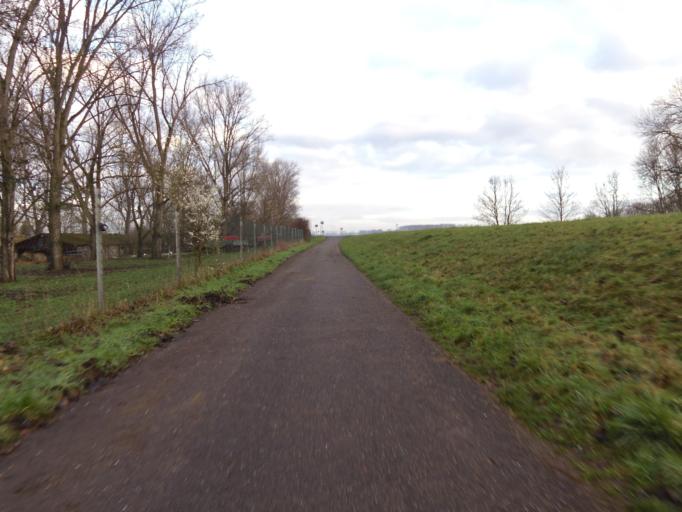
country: DE
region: Hesse
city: Lampertheim
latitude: 49.5738
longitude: 8.4189
